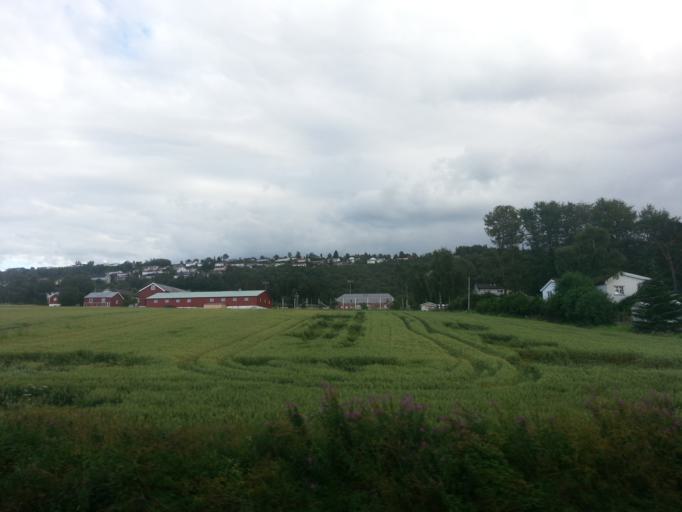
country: NO
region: Sor-Trondelag
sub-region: Malvik
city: Malvik
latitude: 63.4401
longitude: 10.6295
